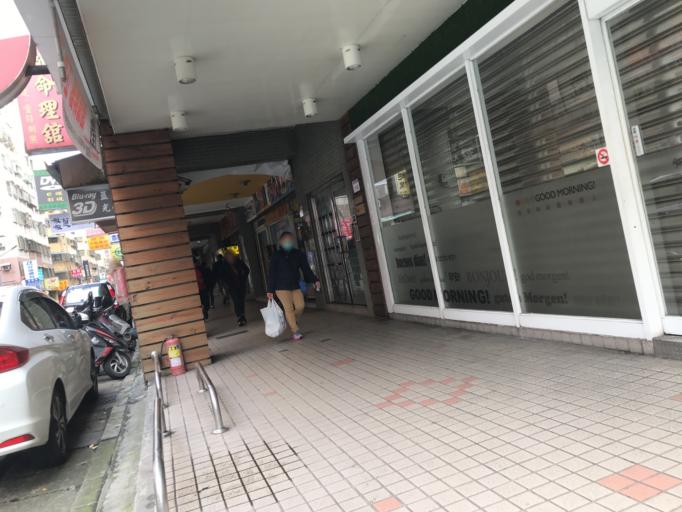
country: TW
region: Taiwan
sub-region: Taoyuan
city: Taoyuan
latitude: 24.9636
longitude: 121.3041
